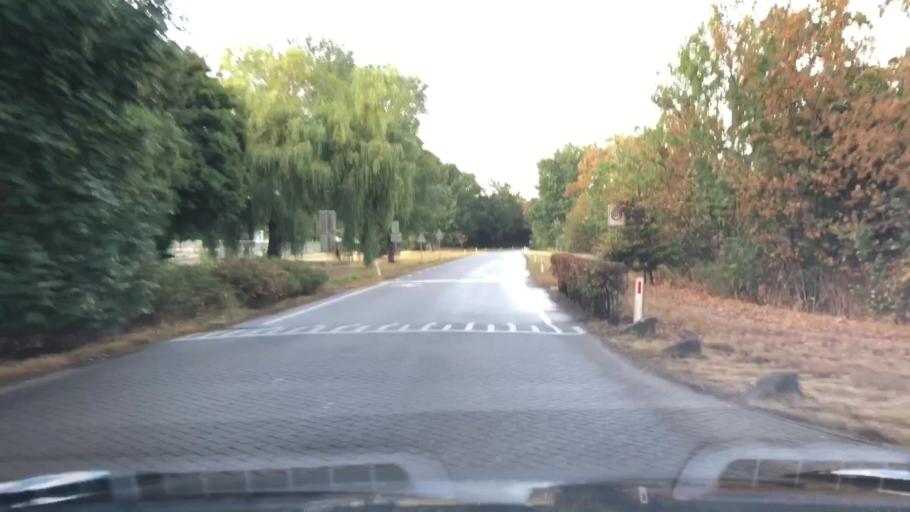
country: NL
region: North Holland
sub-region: Gemeente Naarden
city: Naarden
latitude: 52.3133
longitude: 5.1460
